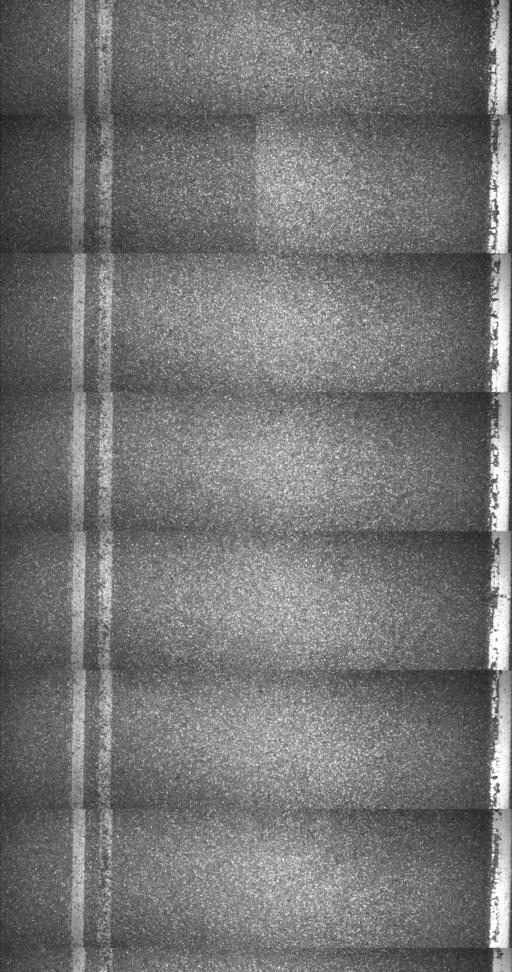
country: US
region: Vermont
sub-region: Addison County
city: Middlebury (village)
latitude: 44.0151
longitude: -73.1019
